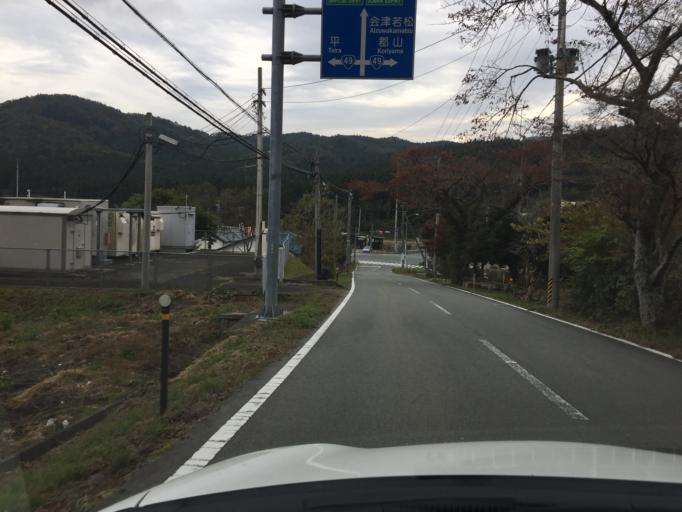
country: JP
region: Fukushima
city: Iwaki
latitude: 37.1026
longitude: 140.7745
